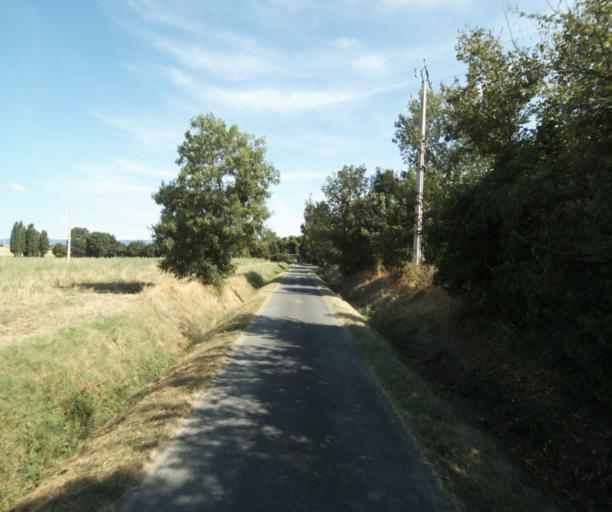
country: FR
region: Midi-Pyrenees
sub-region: Departement de la Haute-Garonne
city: Revel
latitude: 43.5081
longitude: 1.9839
